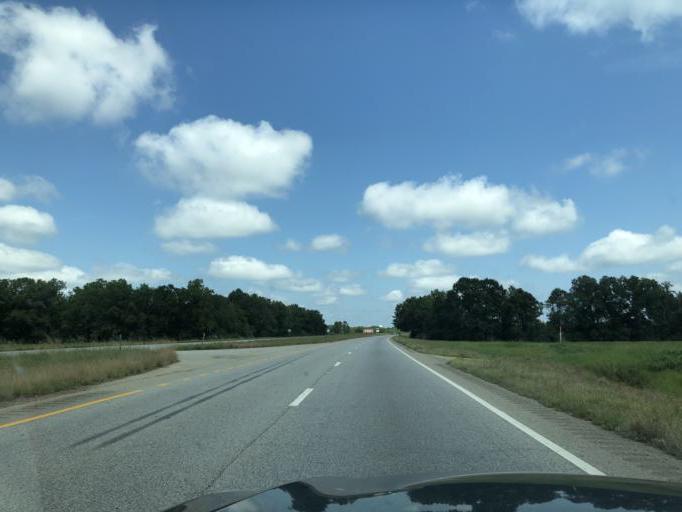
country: US
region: Alabama
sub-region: Henry County
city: Abbeville
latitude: 31.5306
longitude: -85.2912
